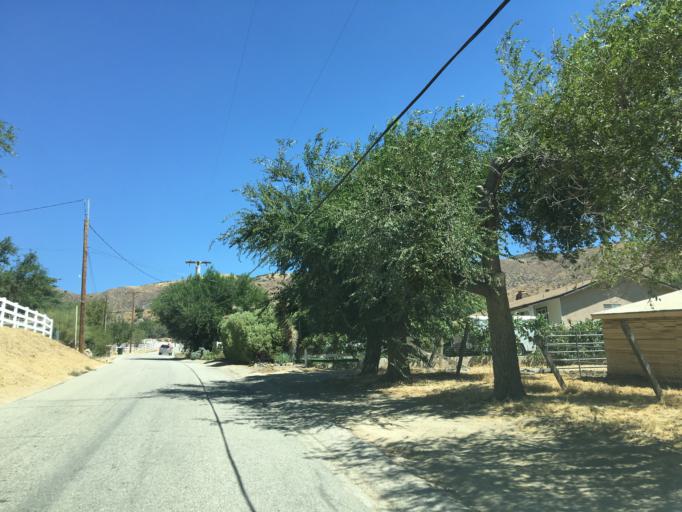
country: US
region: California
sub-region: Los Angeles County
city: Leona Valley
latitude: 34.6193
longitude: -118.2887
